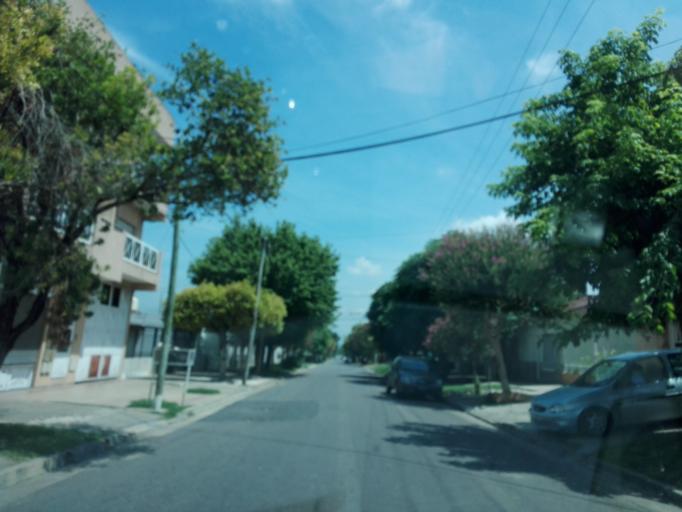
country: AR
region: Buenos Aires
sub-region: Partido de La Plata
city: La Plata
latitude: -34.9450
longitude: -57.9856
